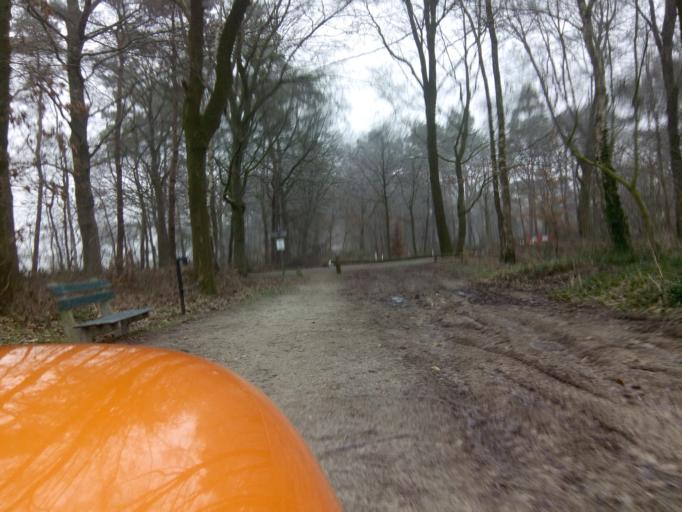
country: NL
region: Gelderland
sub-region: Gemeente Barneveld
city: Voorthuizen
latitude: 52.1978
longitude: 5.5781
